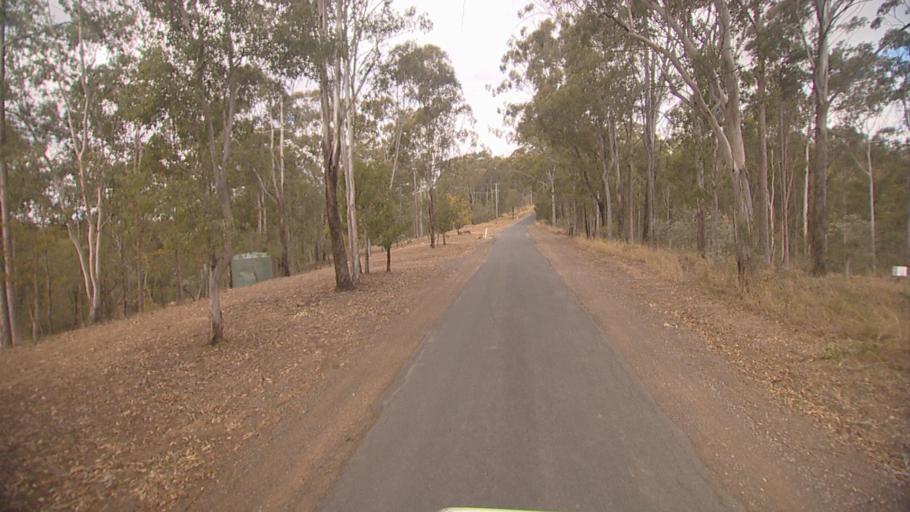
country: AU
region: Queensland
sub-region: Logan
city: Cedar Vale
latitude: -27.8927
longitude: 153.0326
